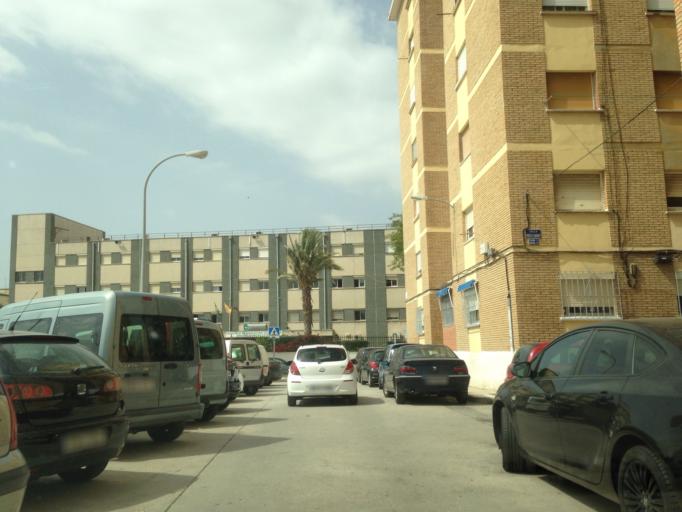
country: ES
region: Andalusia
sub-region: Provincia de Malaga
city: Malaga
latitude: 36.7084
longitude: -4.4409
